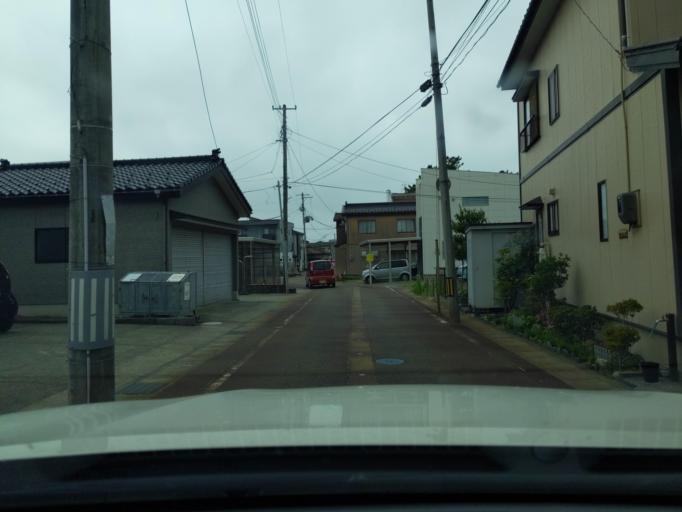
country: JP
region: Niigata
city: Kashiwazaki
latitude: 37.3716
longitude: 138.5668
